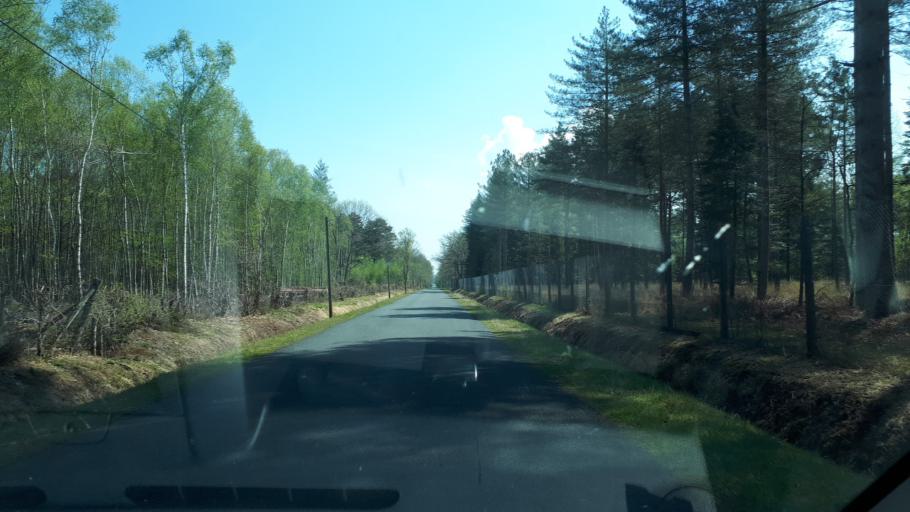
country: FR
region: Centre
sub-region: Departement du Cher
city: Neuvy-sur-Barangeon
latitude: 47.3177
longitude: 2.2277
